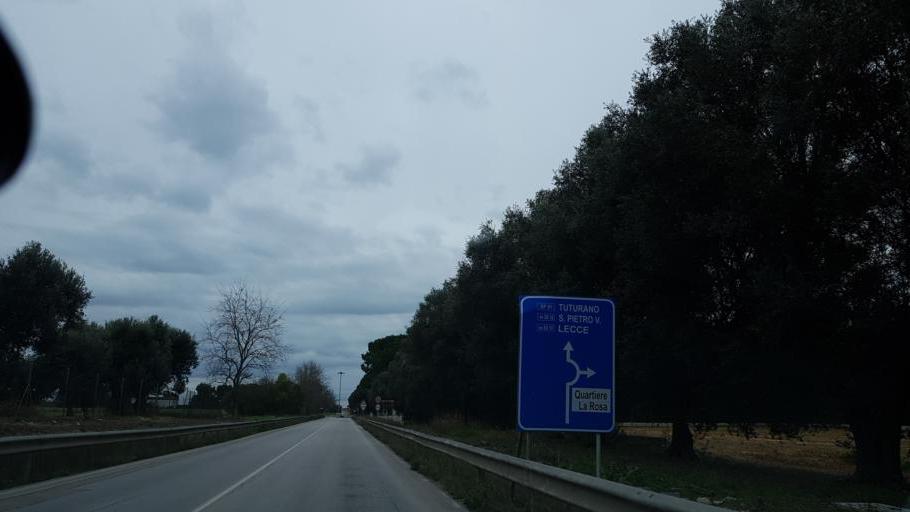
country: IT
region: Apulia
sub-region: Provincia di Brindisi
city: La Rosa
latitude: 40.6119
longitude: 17.9530
